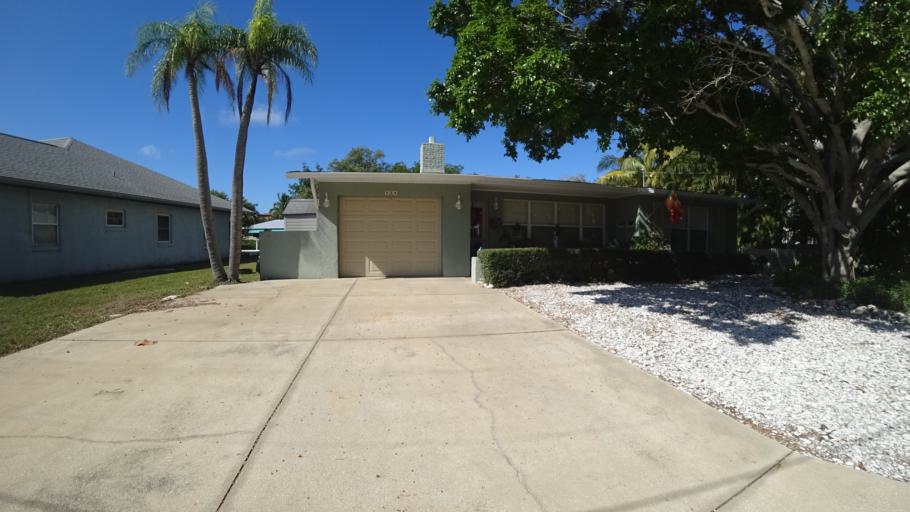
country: US
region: Florida
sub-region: Manatee County
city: Holmes Beach
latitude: 27.5094
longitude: -82.7117
